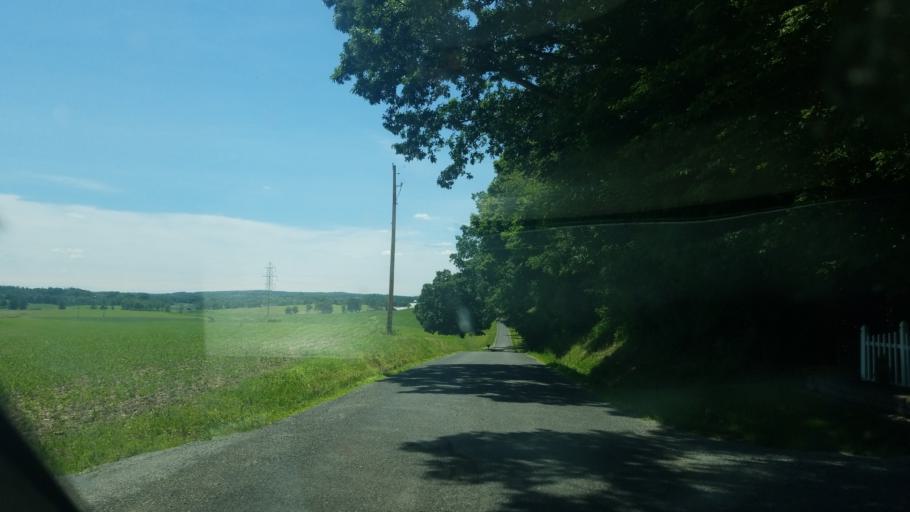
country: US
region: Ohio
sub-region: Mahoning County
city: Sebring
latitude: 40.8654
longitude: -80.9698
